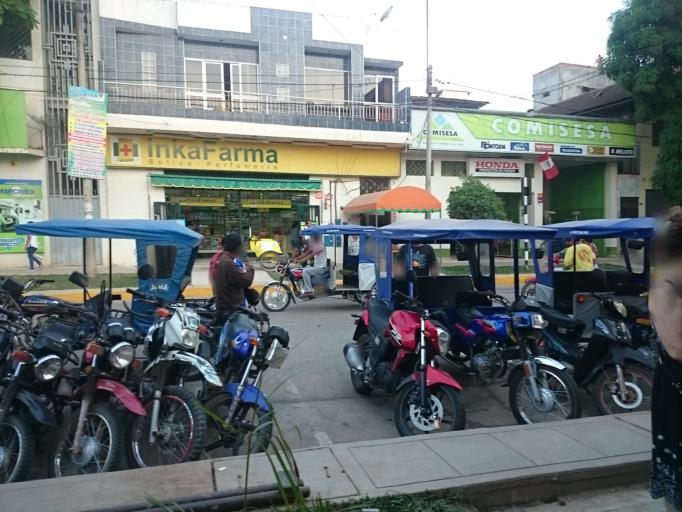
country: PE
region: Ucayali
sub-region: Provincia de Coronel Portillo
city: Pucallpa
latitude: -8.3848
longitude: -74.5300
